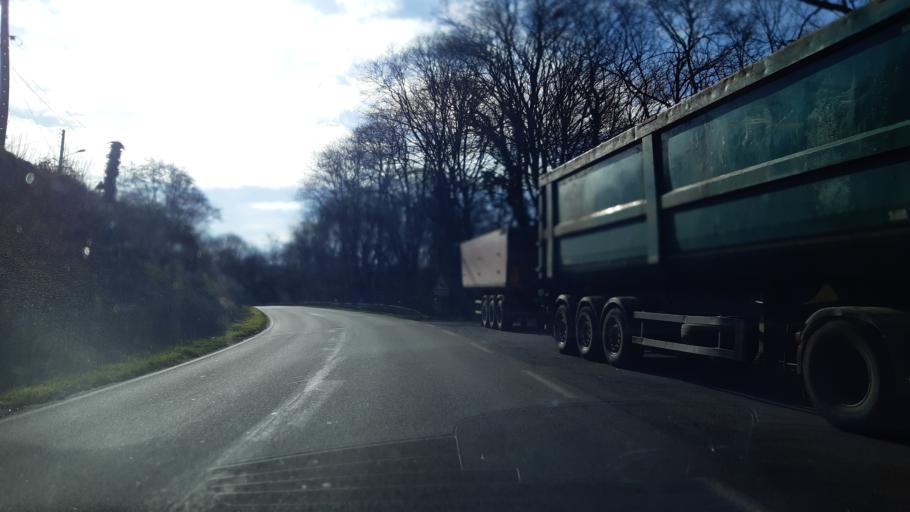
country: FR
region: Lorraine
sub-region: Departement de la Moselle
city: Audun-le-Tiche
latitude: 49.4651
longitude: 5.9597
